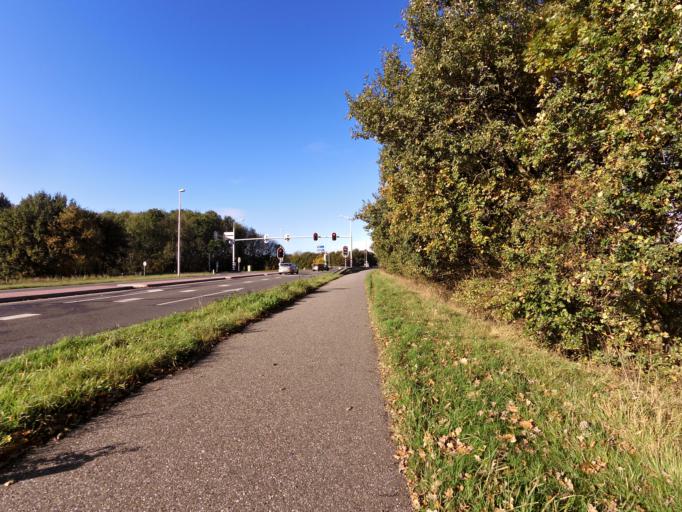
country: NL
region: Gelderland
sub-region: Gemeente Doetinchem
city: Doetinchem
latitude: 51.9436
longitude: 6.2213
